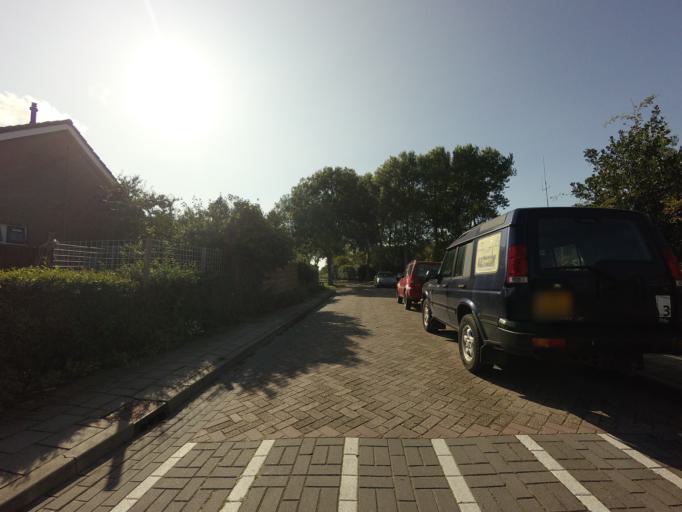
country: NL
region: Friesland
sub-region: Gemeente Terschelling
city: West-Terschelling
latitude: 53.3840
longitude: 5.2828
